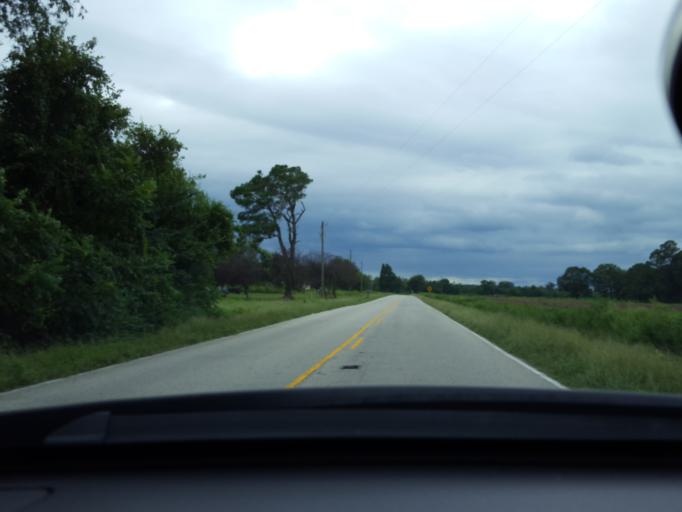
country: US
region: North Carolina
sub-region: Duplin County
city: Rose Hill
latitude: 34.8269
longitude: -78.1557
